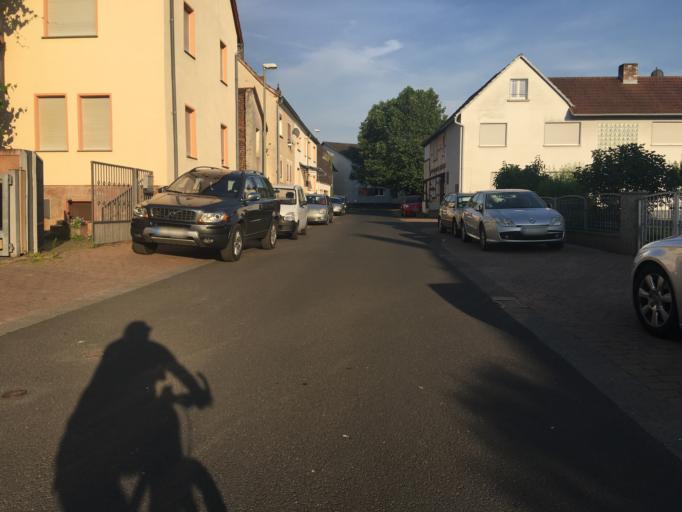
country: DE
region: Hesse
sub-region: Regierungsbezirk Darmstadt
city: Gelnhausen
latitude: 50.1899
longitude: 9.1554
